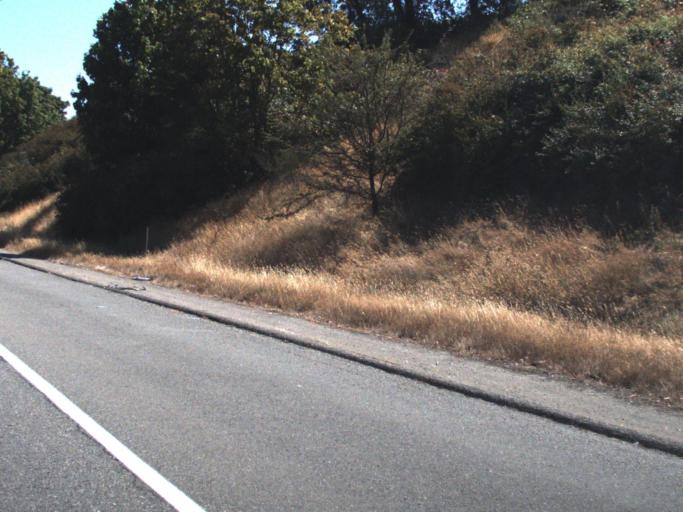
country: US
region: Washington
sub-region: King County
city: Riverton
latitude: 47.4677
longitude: -122.3060
